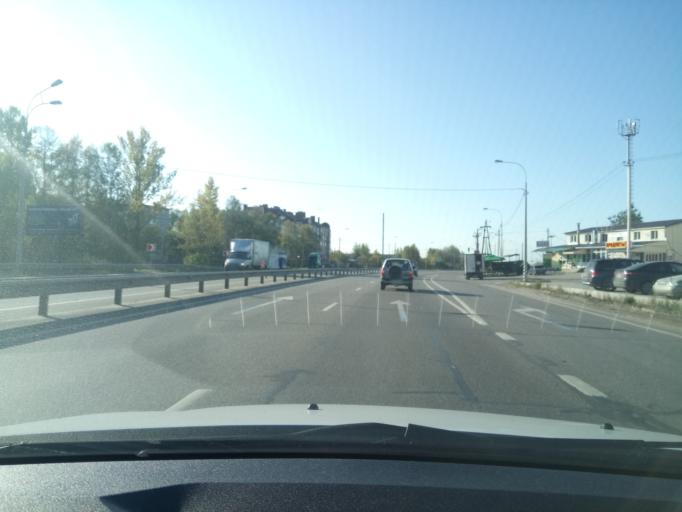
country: RU
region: Nizjnij Novgorod
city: Burevestnik
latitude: 56.1646
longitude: 43.9160
